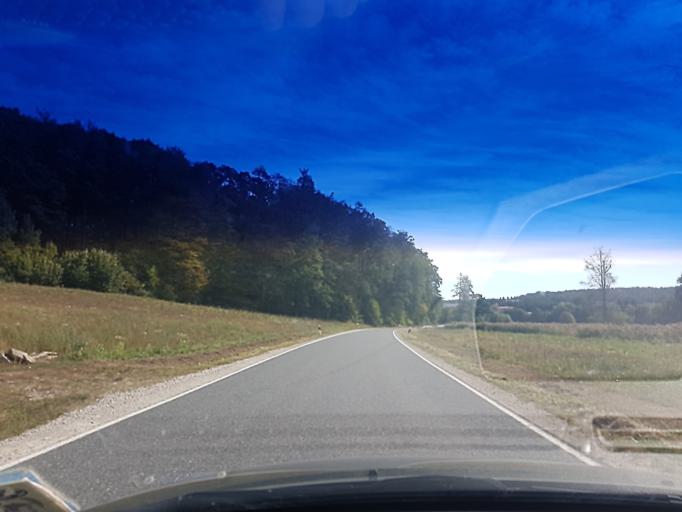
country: DE
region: Bavaria
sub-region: Regierungsbezirk Mittelfranken
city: Wachenroth
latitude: 49.7758
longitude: 10.7124
